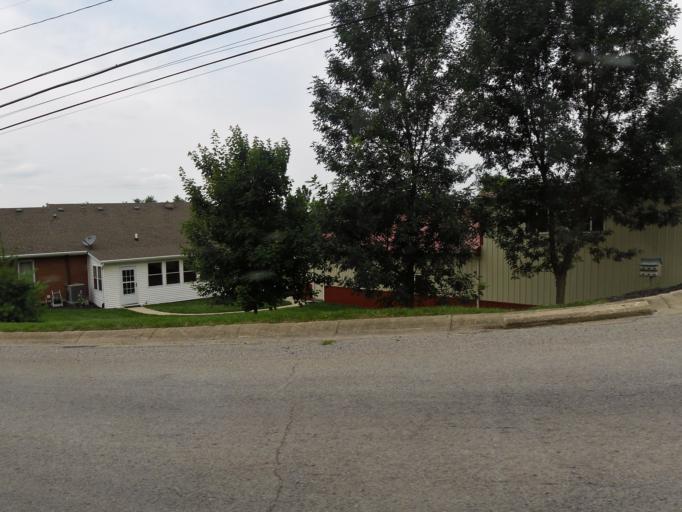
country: US
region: Ohio
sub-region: Warren County
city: Waynesville
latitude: 39.5248
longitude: -84.0778
